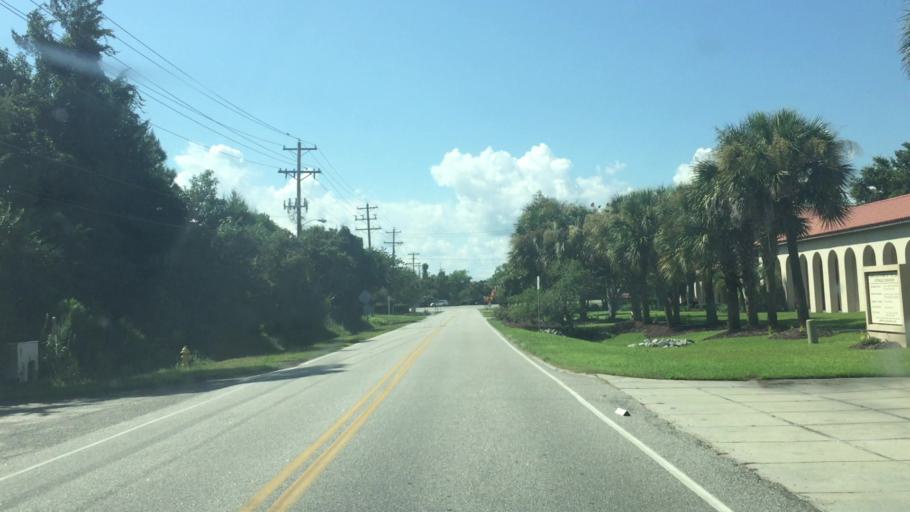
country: US
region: South Carolina
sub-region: Horry County
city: North Myrtle Beach
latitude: 33.8335
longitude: -78.6701
